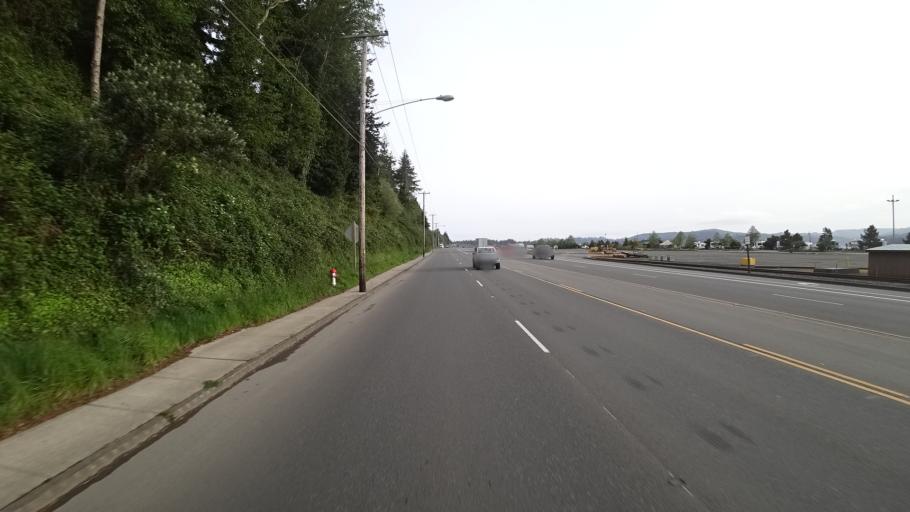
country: US
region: Oregon
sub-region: Coos County
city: North Bend
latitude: 43.3963
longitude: -124.2202
